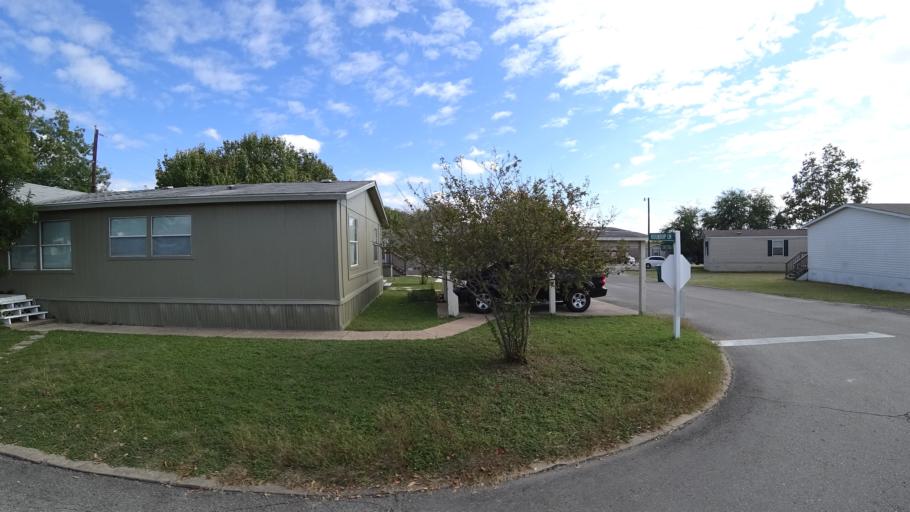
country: US
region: Texas
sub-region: Travis County
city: Pflugerville
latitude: 30.4343
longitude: -97.6402
